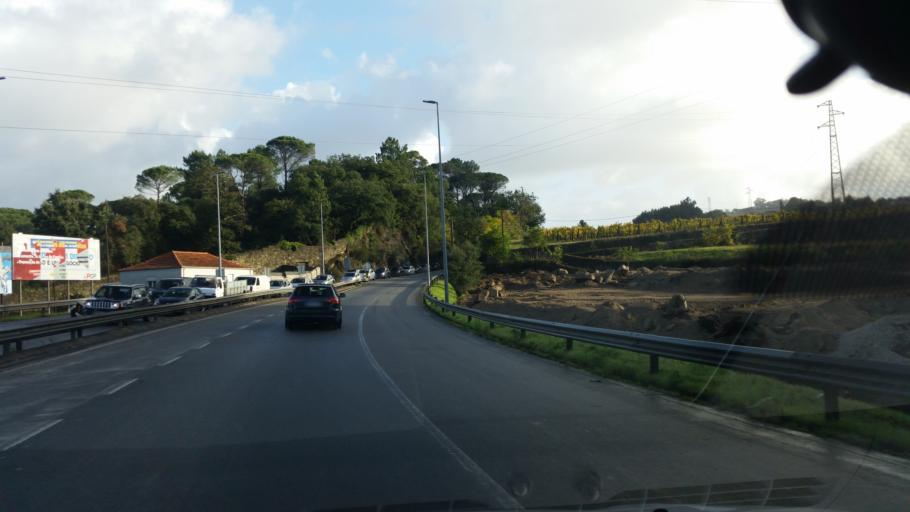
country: PT
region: Porto
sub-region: Santo Tirso
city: Santo Tirso
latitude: 41.3427
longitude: -8.4674
